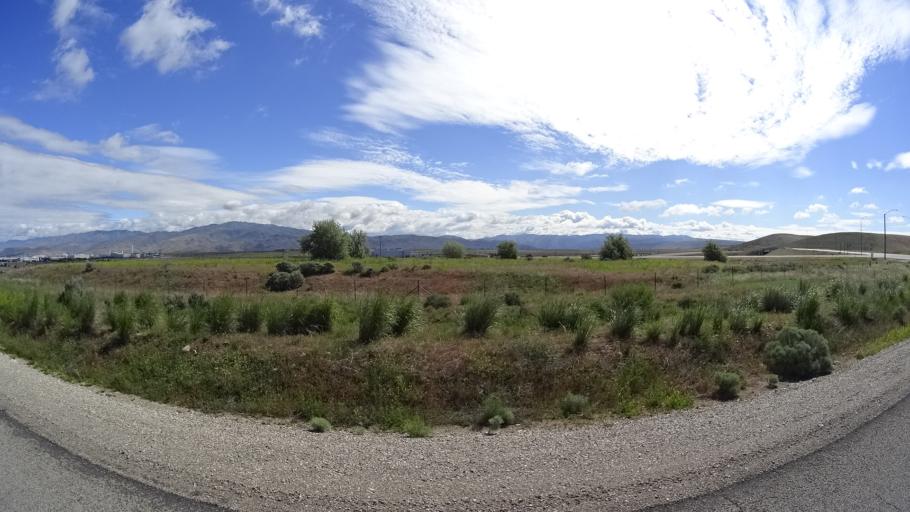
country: US
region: Idaho
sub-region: Ada County
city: Boise
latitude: 43.5082
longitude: -116.1473
